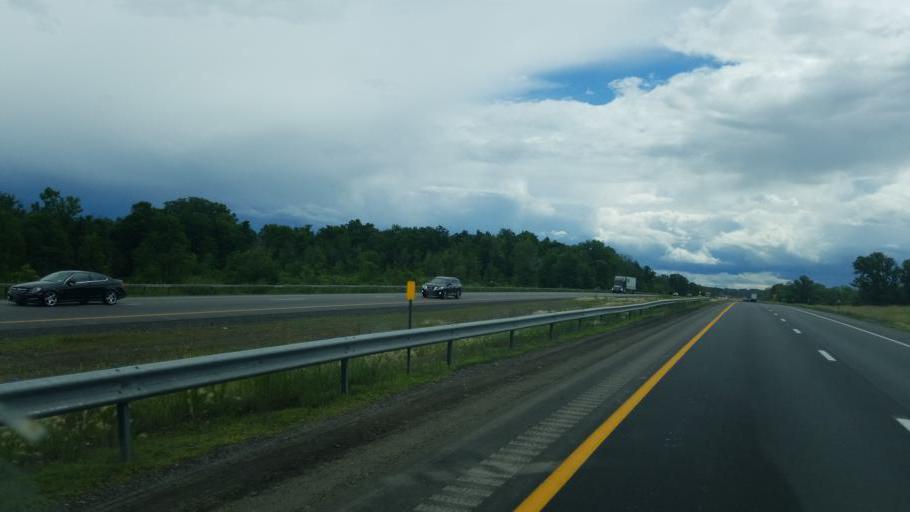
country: US
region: New York
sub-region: Livingston County
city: Caledonia
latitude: 43.0297
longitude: -77.8602
